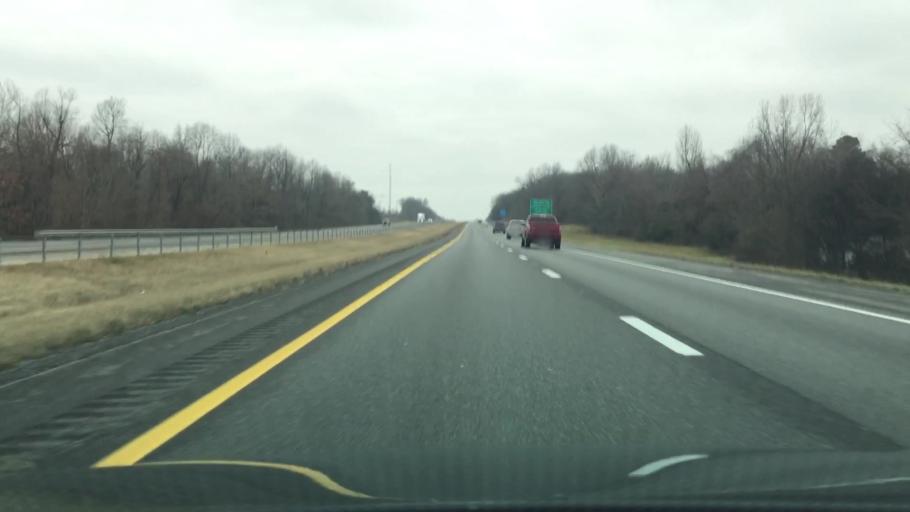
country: US
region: Kentucky
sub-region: McCracken County
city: Hendron
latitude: 37.0378
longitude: -88.6322
